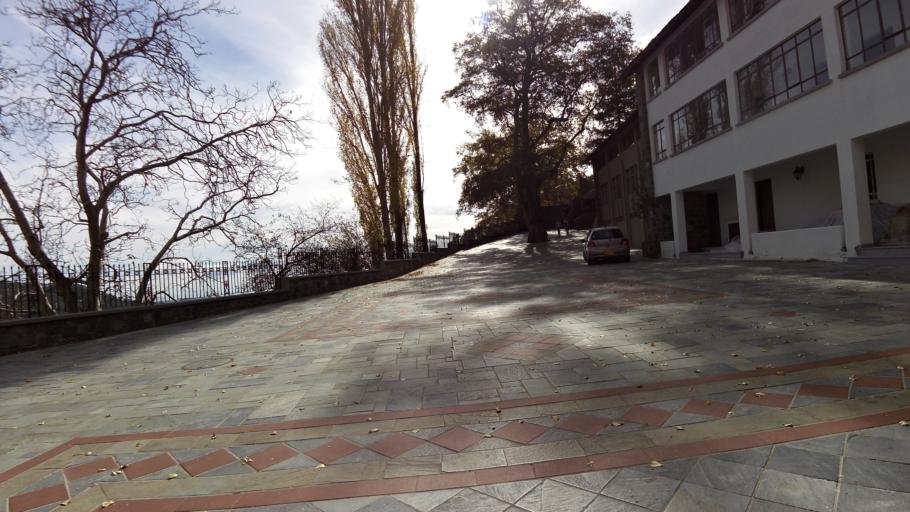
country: CY
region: Lefkosia
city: Kakopetria
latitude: 34.9126
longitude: 32.8383
